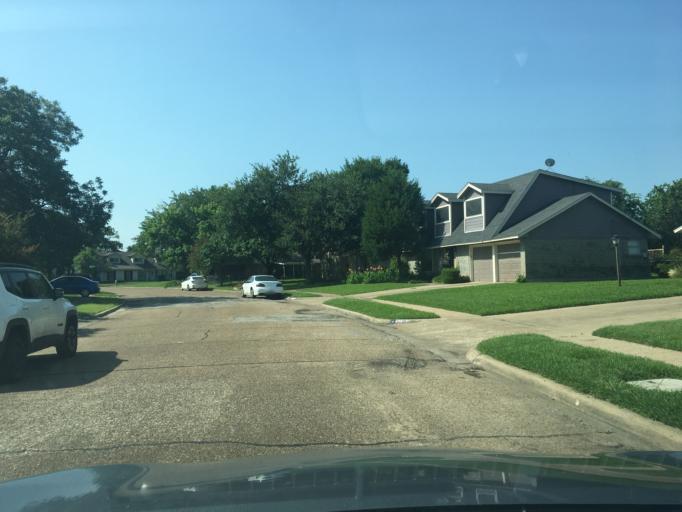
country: US
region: Texas
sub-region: Dallas County
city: Richardson
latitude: 32.9265
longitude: -96.6974
